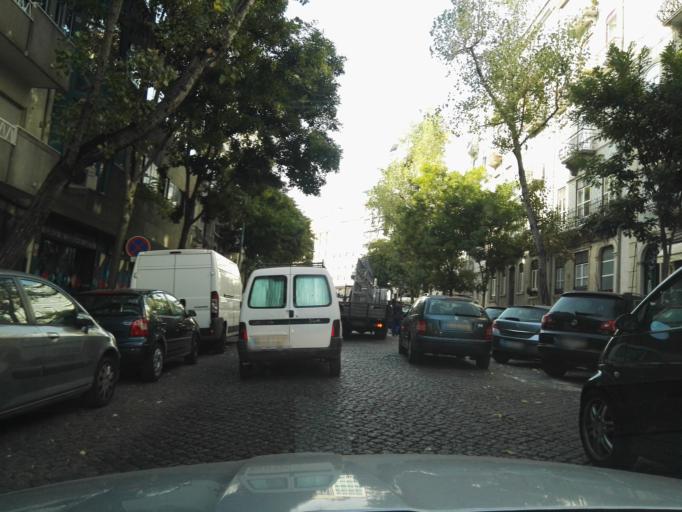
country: PT
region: Lisbon
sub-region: Lisbon
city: Lisbon
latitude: 38.7279
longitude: -9.1436
